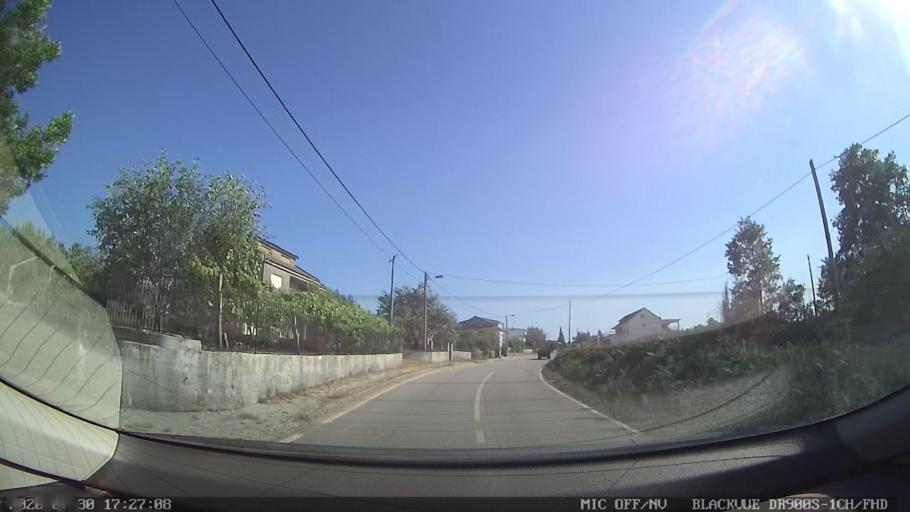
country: PT
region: Vila Real
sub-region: Murca
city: Murca
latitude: 41.3222
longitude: -7.4615
